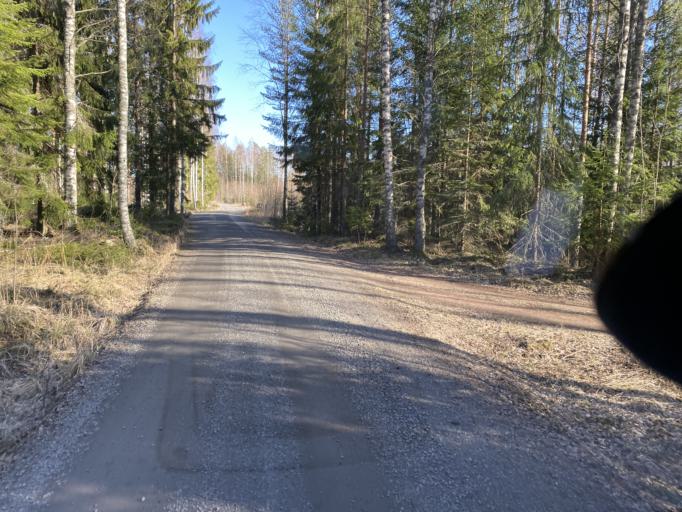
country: FI
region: Satakunta
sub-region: Rauma
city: Lappi
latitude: 61.1483
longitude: 21.8919
